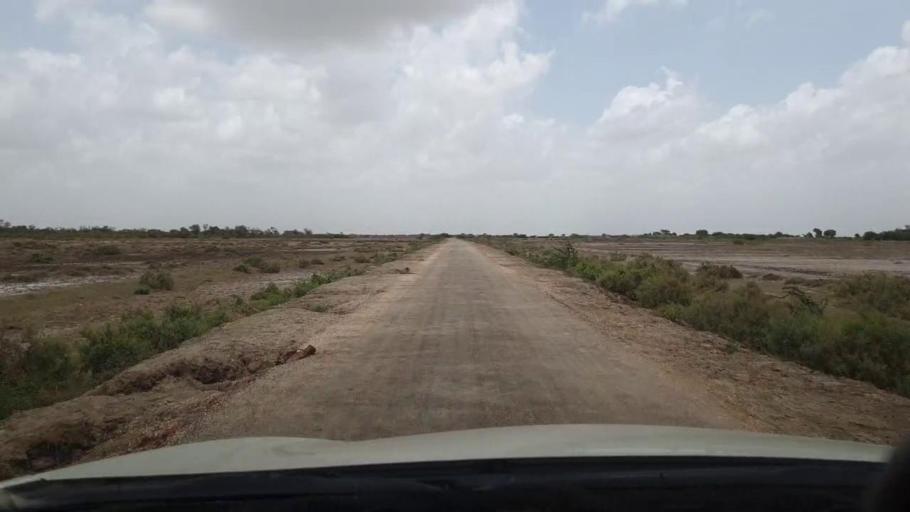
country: PK
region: Sindh
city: Kadhan
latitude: 24.3602
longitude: 68.9308
